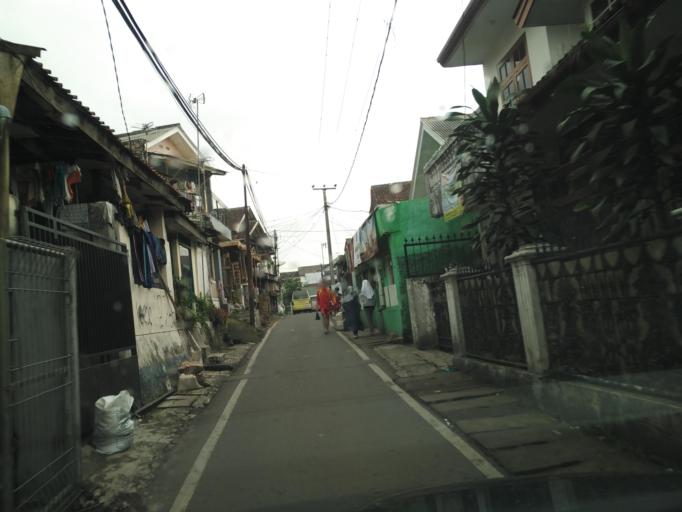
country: ID
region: West Java
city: Sukabumi
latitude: -6.7314
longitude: 107.0380
